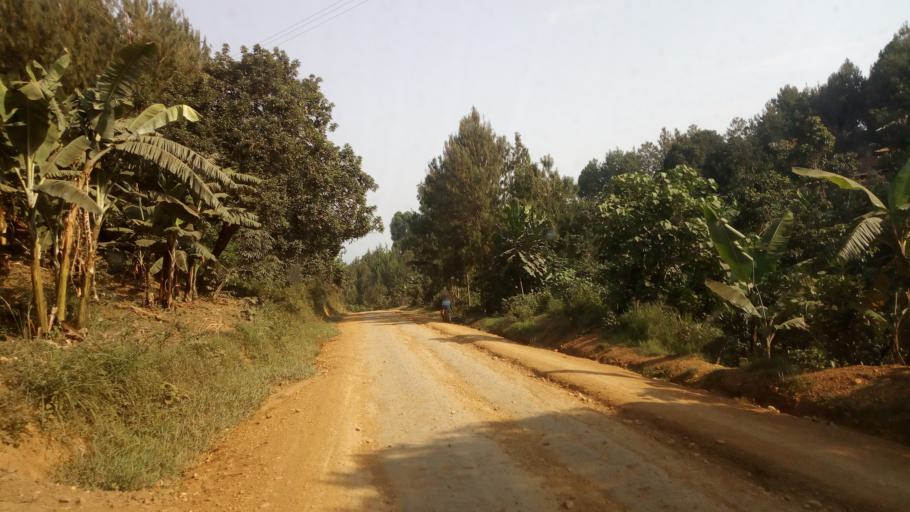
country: UG
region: Western Region
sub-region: Kanungu District
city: Ntungamo
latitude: -0.8280
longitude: 29.7073
